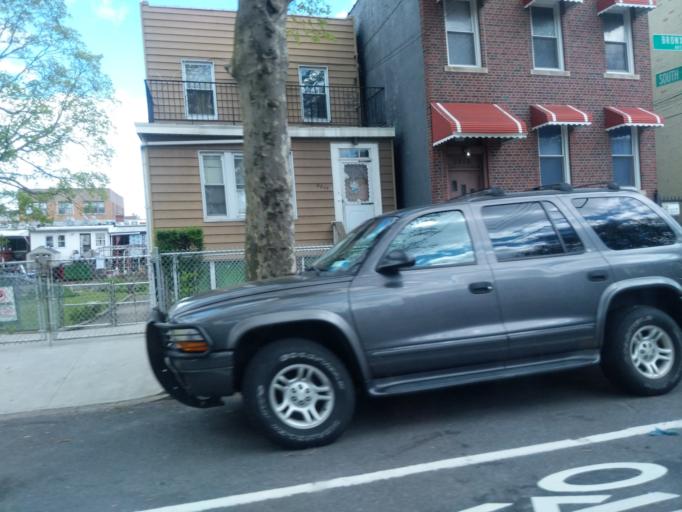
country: US
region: New York
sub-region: Bronx
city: The Bronx
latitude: 40.8719
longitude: -73.8613
